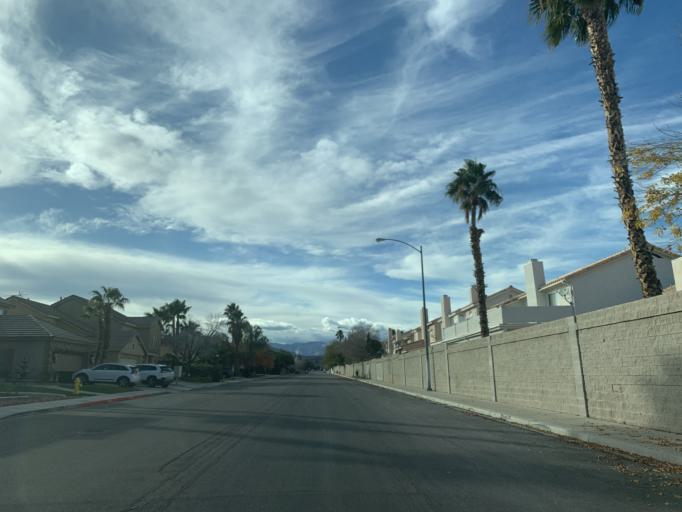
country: US
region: Nevada
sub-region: Clark County
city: Summerlin South
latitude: 36.1280
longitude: -115.3007
